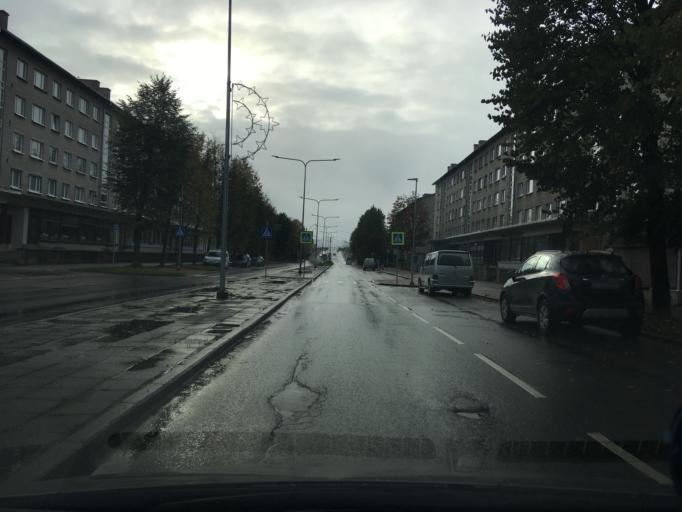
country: EE
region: Ida-Virumaa
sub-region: Narva linn
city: Narva
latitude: 59.3766
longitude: 28.1808
